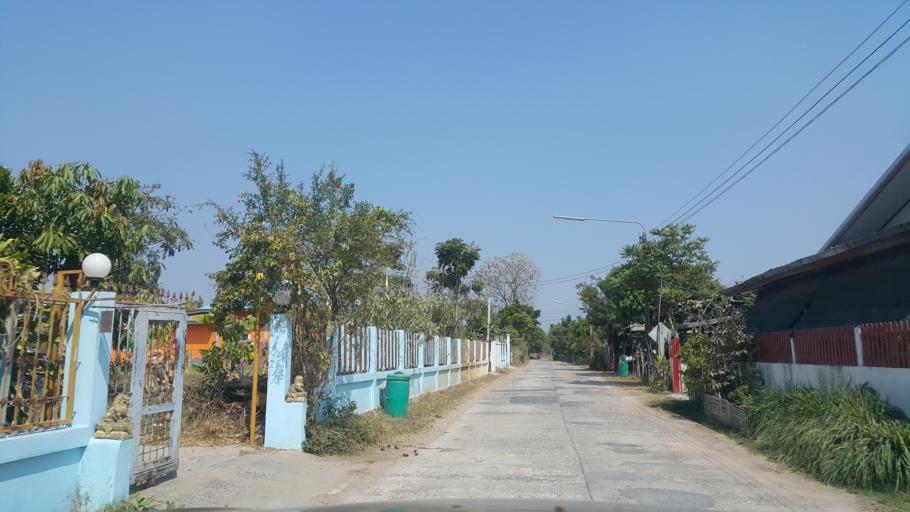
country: TH
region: Buriram
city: Satuek
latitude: 15.1342
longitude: 103.3455
